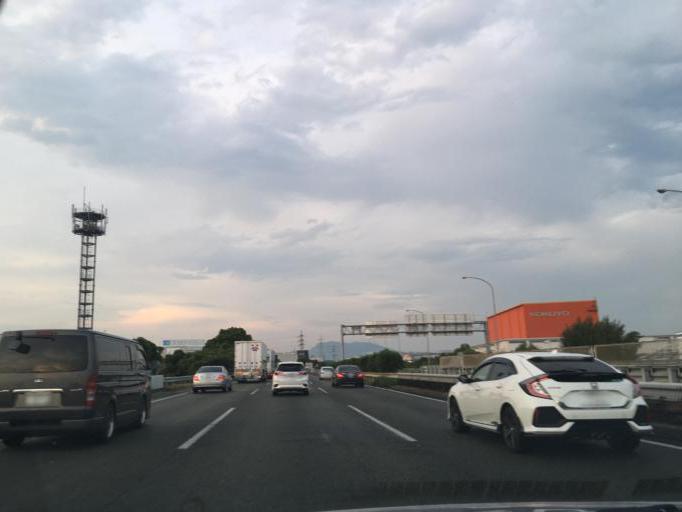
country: JP
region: Saga Prefecture
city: Tosu
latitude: 33.4083
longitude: 130.5381
